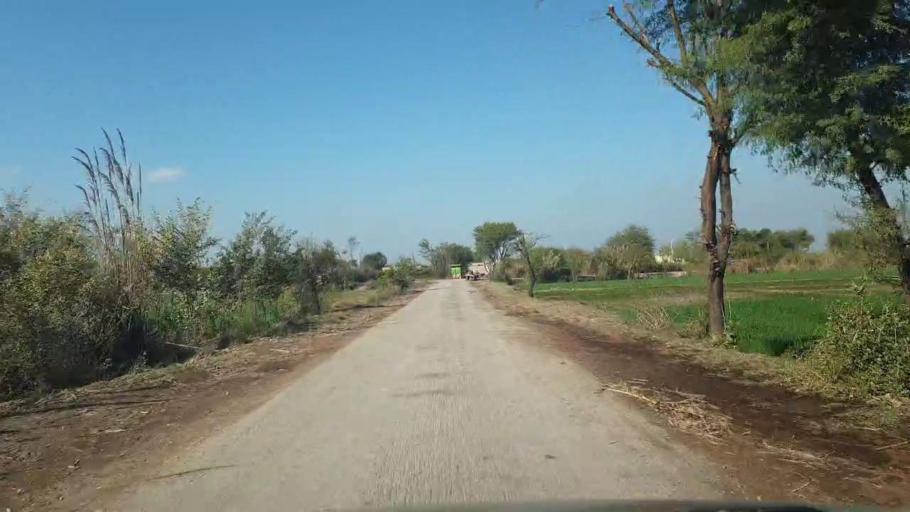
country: PK
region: Sindh
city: Shahdadpur
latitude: 25.9145
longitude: 68.5330
